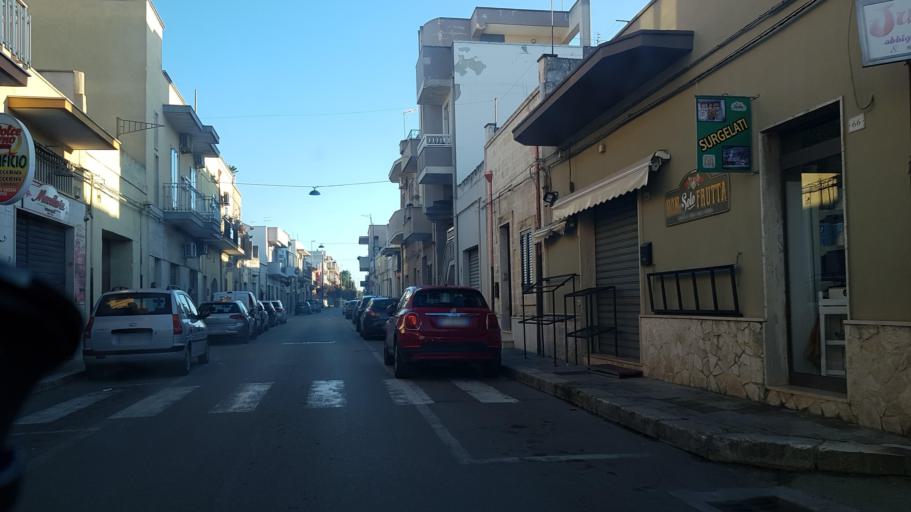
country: IT
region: Apulia
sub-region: Provincia di Brindisi
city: Latiano
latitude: 40.5502
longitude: 17.7181
